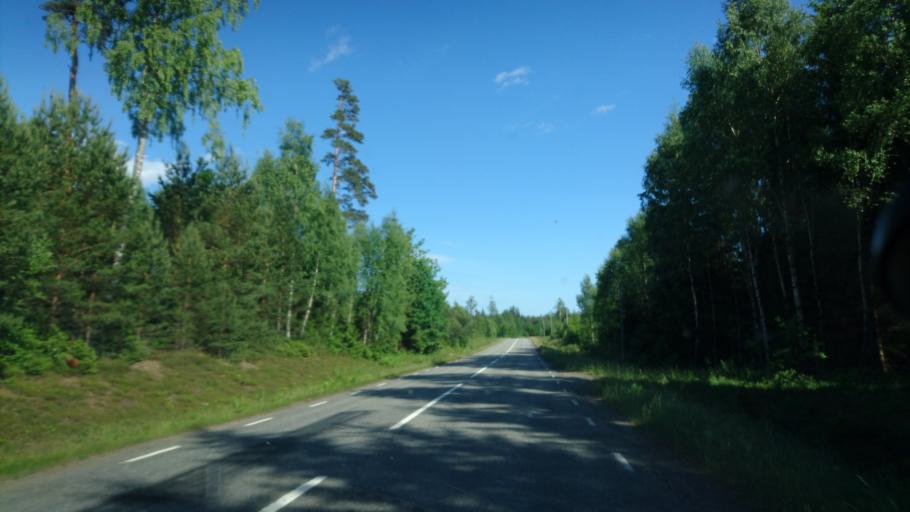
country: SE
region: Skane
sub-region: Osby Kommun
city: Lonsboda
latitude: 56.4254
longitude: 14.2774
